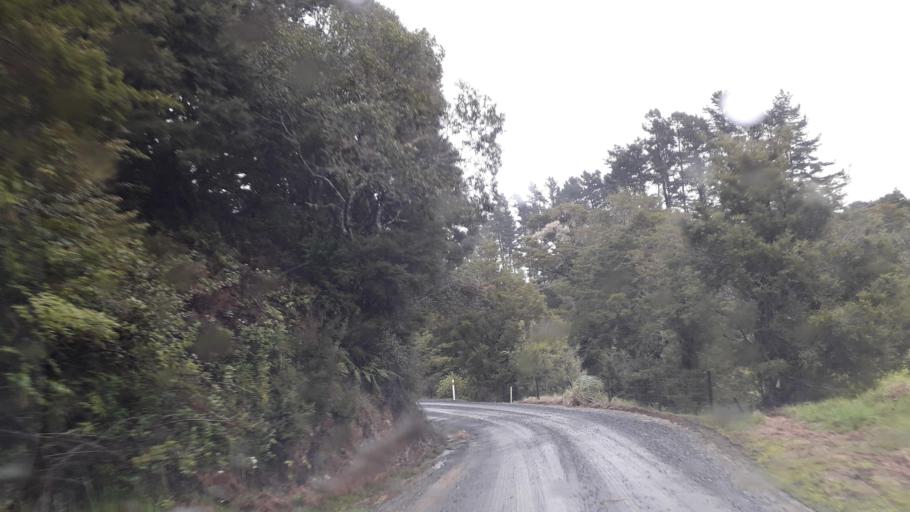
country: NZ
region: Northland
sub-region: Far North District
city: Waimate North
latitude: -35.1323
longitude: 173.7186
